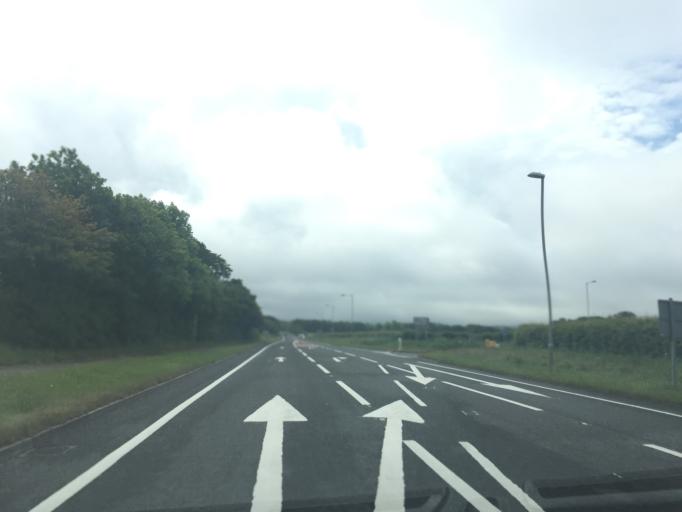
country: GB
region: England
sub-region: Dorset
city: Wareham
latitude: 50.6738
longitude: -2.1117
